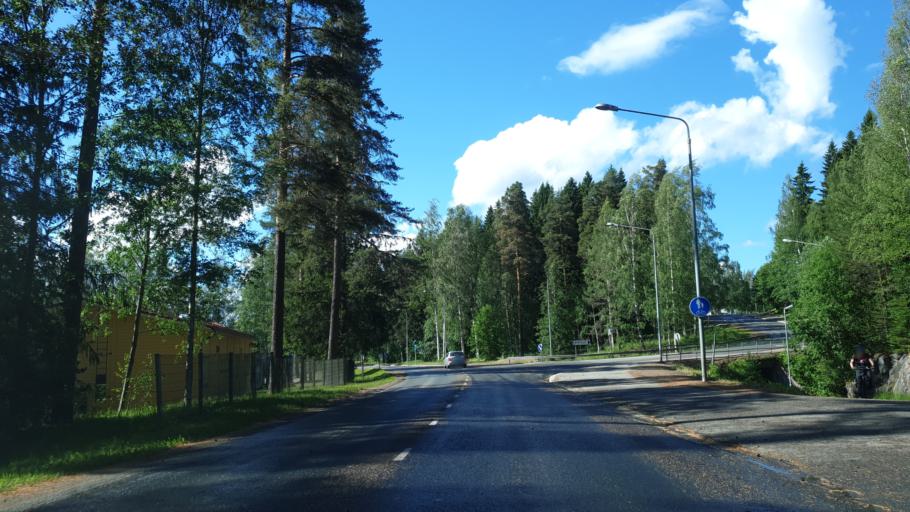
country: FI
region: Northern Savo
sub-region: Kuopio
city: Kuopio
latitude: 62.9149
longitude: 27.6356
